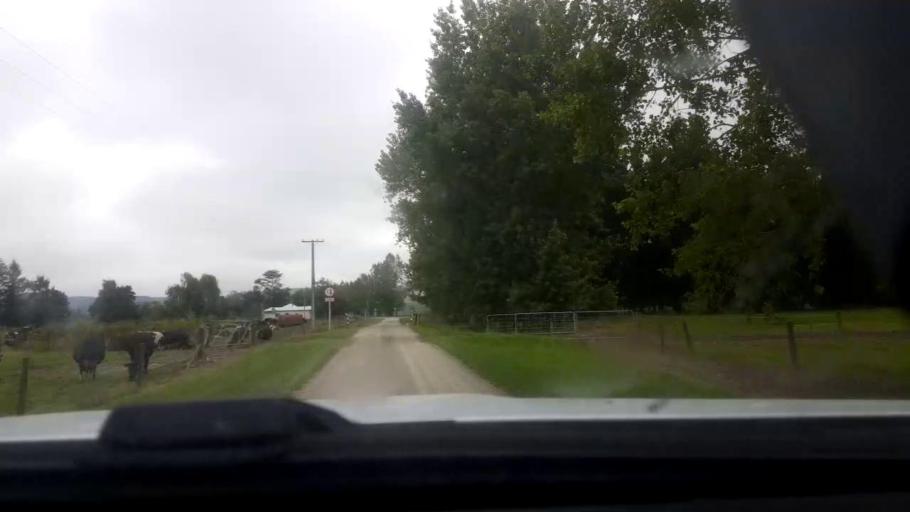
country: NZ
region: Canterbury
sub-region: Timaru District
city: Pleasant Point
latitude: -44.2087
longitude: 171.1122
